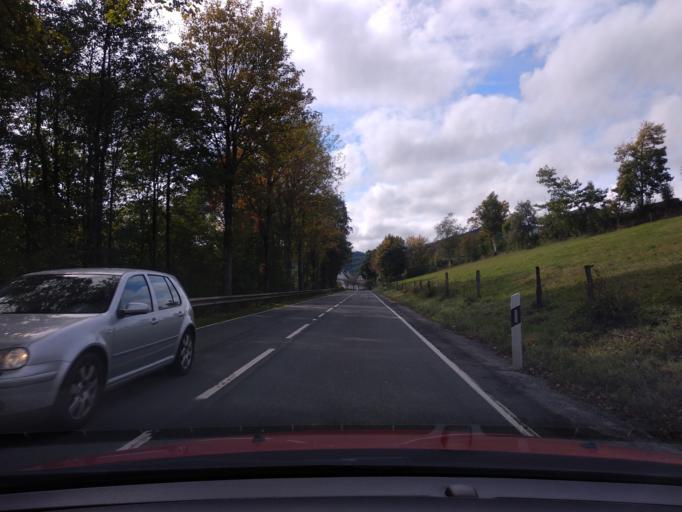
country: DE
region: North Rhine-Westphalia
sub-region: Regierungsbezirk Arnsberg
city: Bad Fredeburg
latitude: 51.2592
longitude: 8.3758
